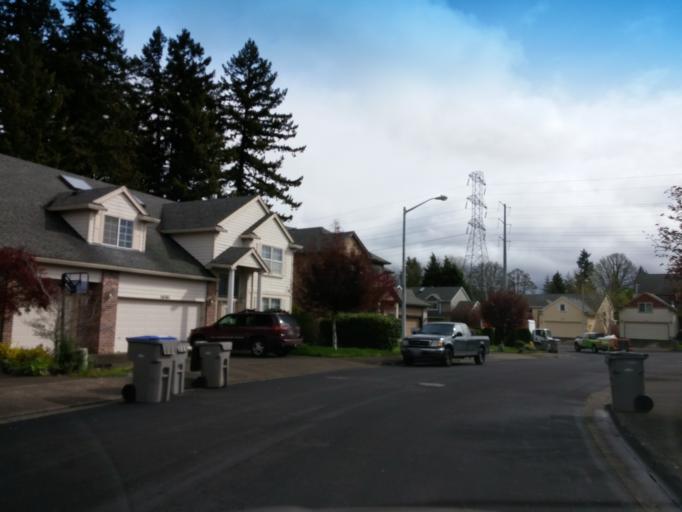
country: US
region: Oregon
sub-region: Washington County
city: Oak Hills
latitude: 45.5400
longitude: -122.8477
